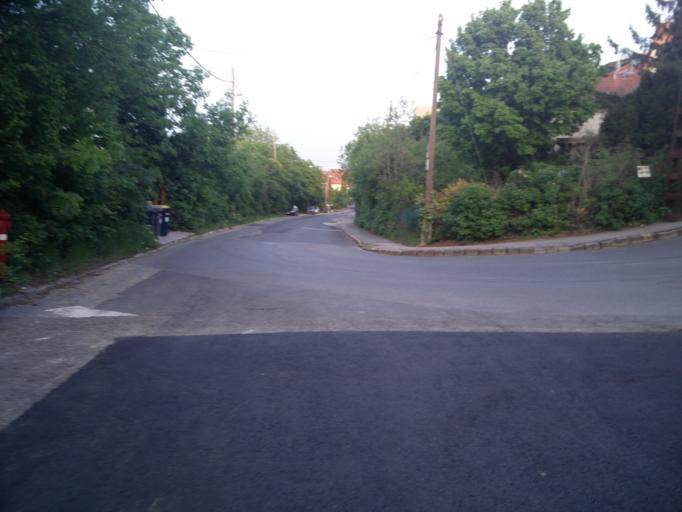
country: HU
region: Budapest
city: Budapest XII. keruelet
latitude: 47.5103
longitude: 18.9923
